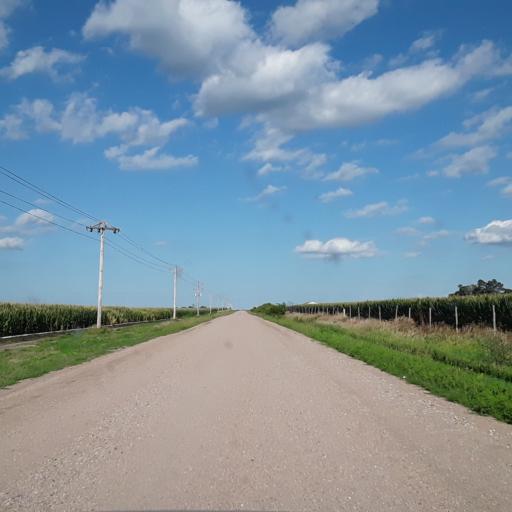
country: US
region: Nebraska
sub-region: Hall County
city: Wood River
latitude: 40.9169
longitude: -98.6071
